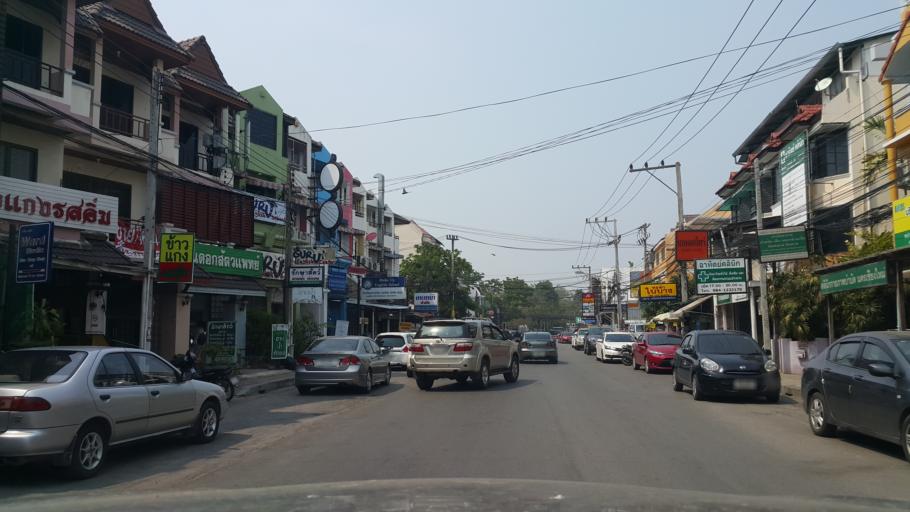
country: TH
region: Chiang Mai
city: Chiang Mai
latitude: 18.7888
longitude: 98.9625
